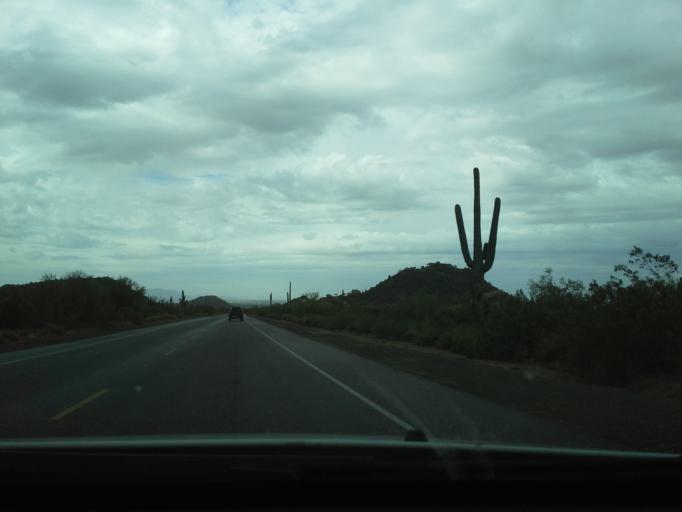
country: US
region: Arizona
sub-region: Pinal County
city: Apache Junction
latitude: 33.4731
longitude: -111.6278
